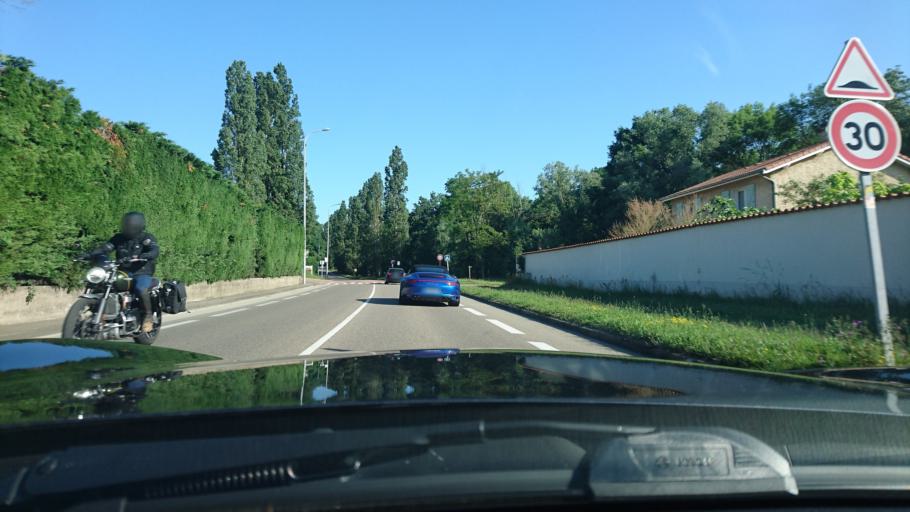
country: FR
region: Rhone-Alpes
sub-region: Departement du Rhone
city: Chaponost
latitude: 45.7042
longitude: 4.7528
